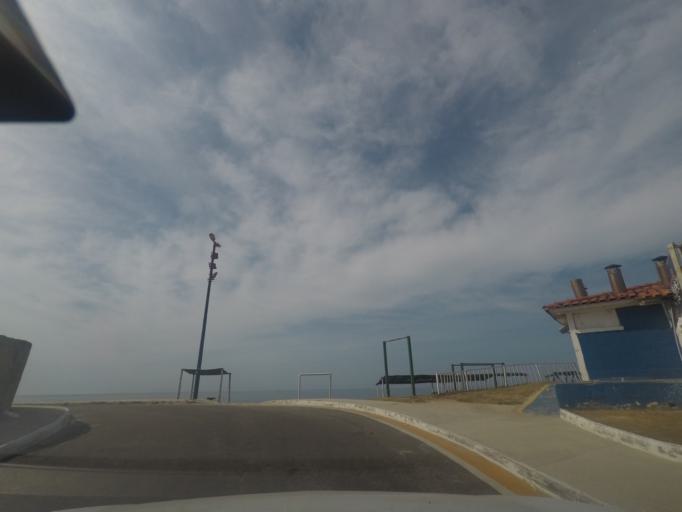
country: BR
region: Rio de Janeiro
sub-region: Marica
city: Marica
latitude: -22.9609
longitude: -42.8165
